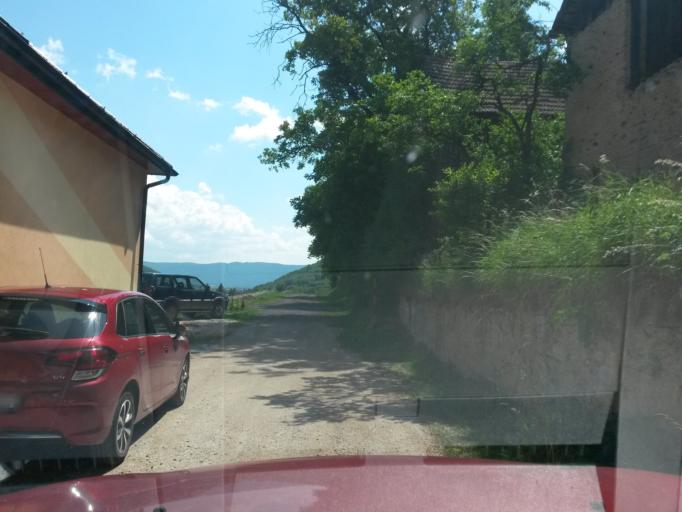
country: SK
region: Kosicky
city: Roznava
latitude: 48.6906
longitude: 20.5406
